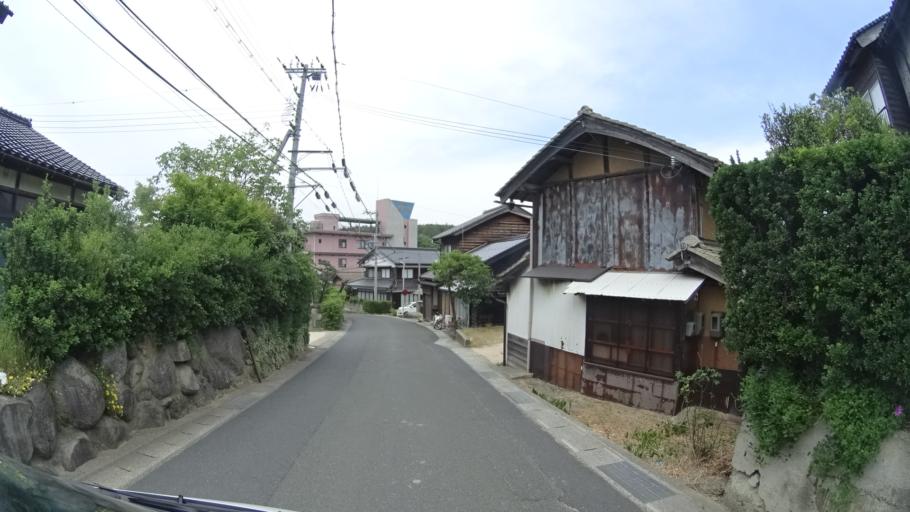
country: JP
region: Kyoto
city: Miyazu
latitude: 35.6973
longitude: 135.0546
